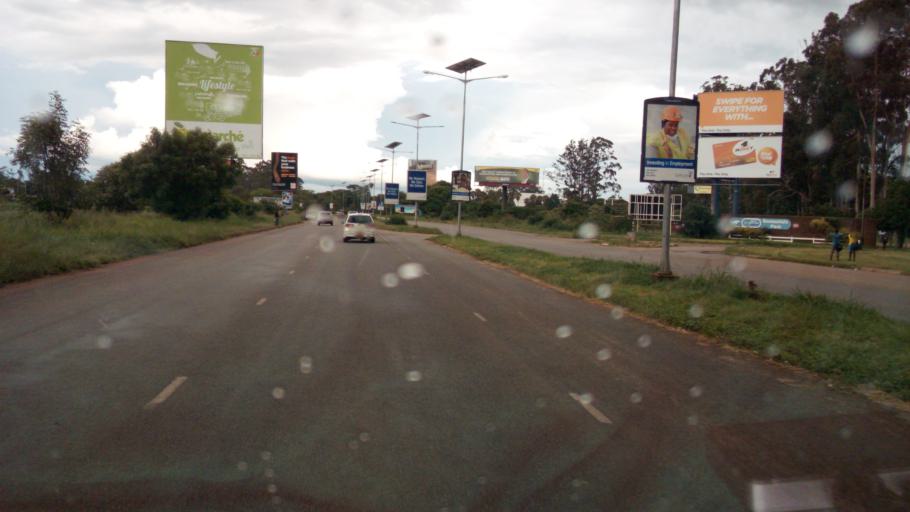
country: ZW
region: Harare
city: Harare
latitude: -17.7801
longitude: 31.0838
